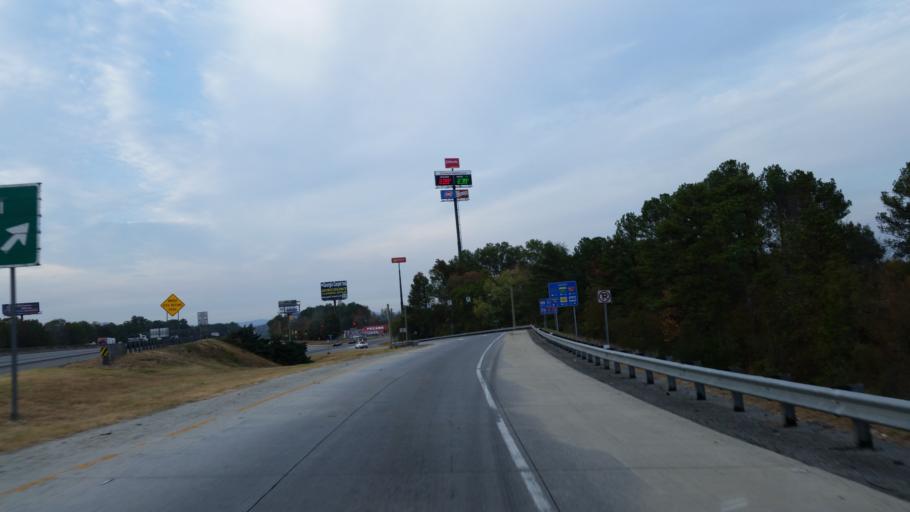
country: US
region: Georgia
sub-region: Gordon County
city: Calhoun
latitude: 34.5559
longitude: -84.9348
